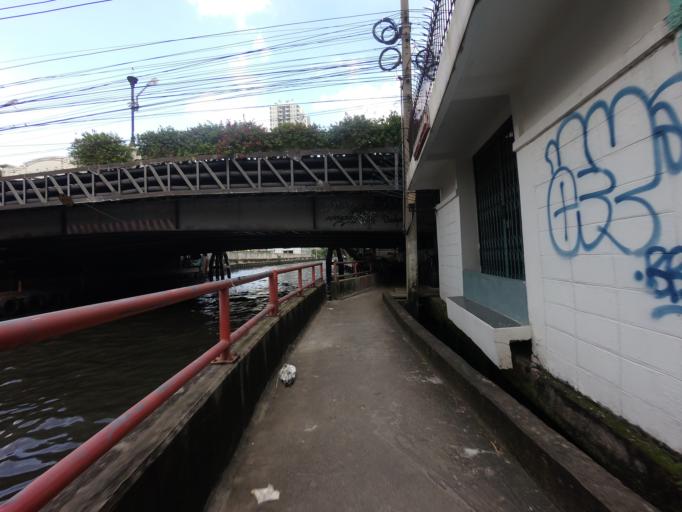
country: TH
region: Bangkok
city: Din Daeng
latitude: 13.7478
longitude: 100.5630
